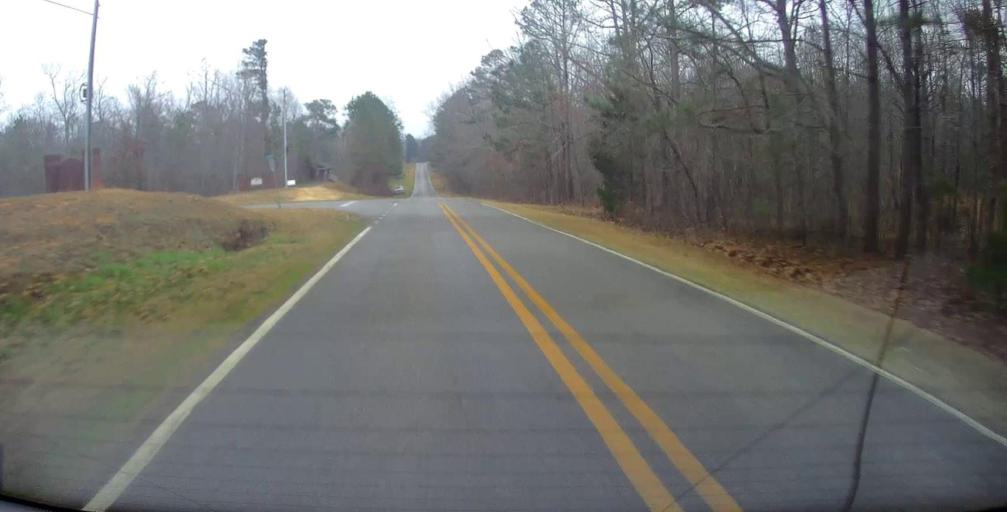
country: US
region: Georgia
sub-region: Lamar County
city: Barnesville
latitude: 33.0673
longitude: -84.1228
